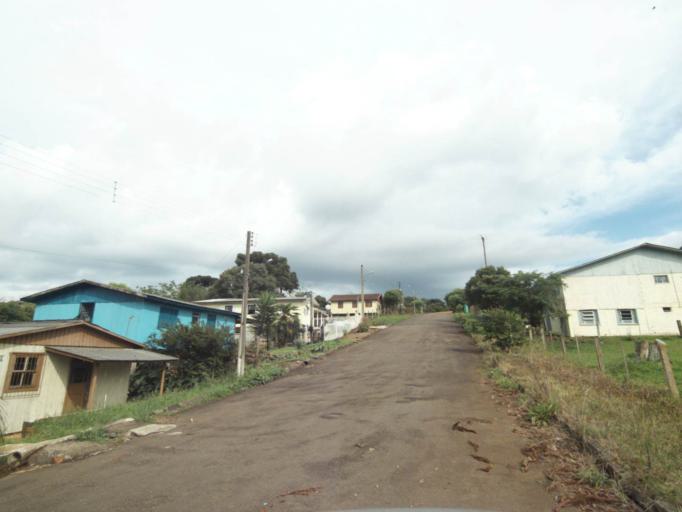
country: BR
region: Rio Grande do Sul
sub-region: Lagoa Vermelha
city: Lagoa Vermelha
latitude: -28.2315
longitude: -51.5083
